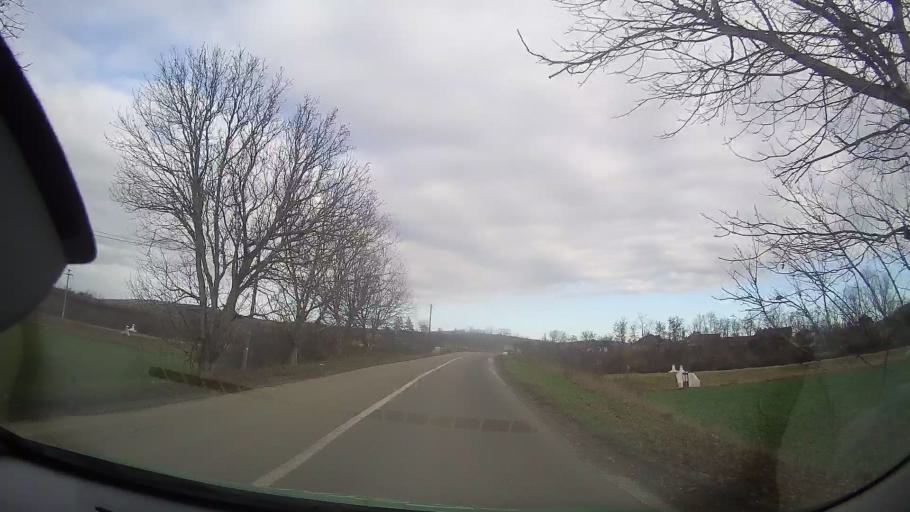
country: RO
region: Mures
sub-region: Comuna Iernut
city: Iernut
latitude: 46.4687
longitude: 24.2182
